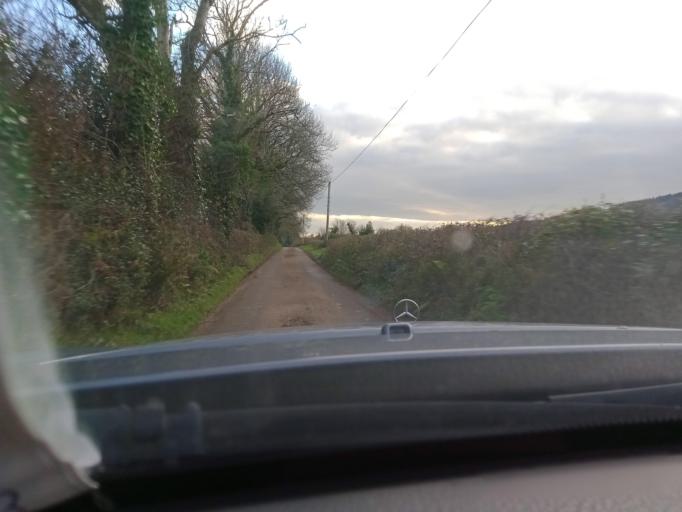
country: IE
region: Leinster
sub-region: Kilkenny
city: Graiguenamanagh
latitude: 52.5148
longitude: -6.9436
